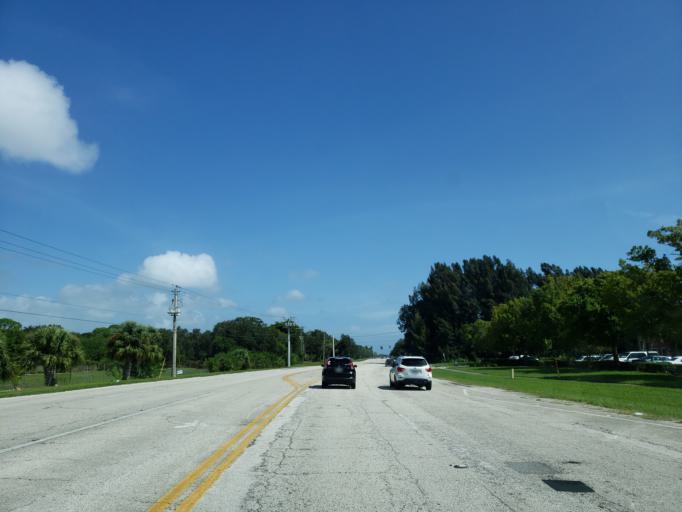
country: US
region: Florida
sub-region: Brevard County
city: West Melbourne
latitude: 28.0835
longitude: -80.6544
